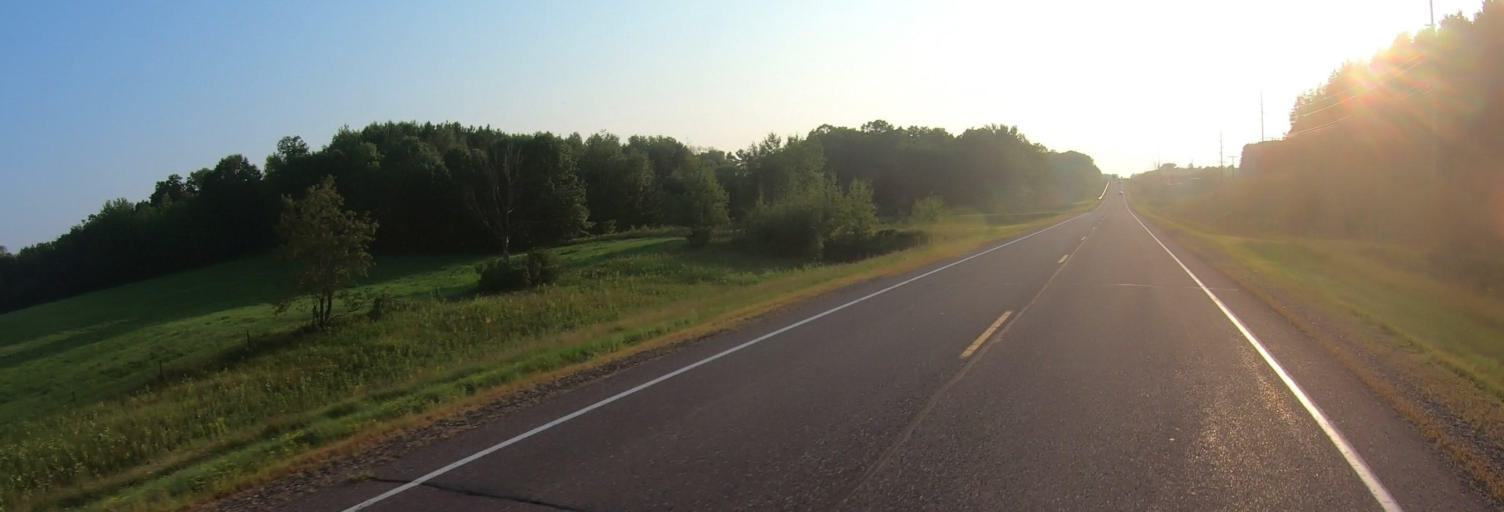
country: US
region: Wisconsin
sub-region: Washburn County
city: Shell Lake
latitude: 45.8154
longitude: -92.0621
